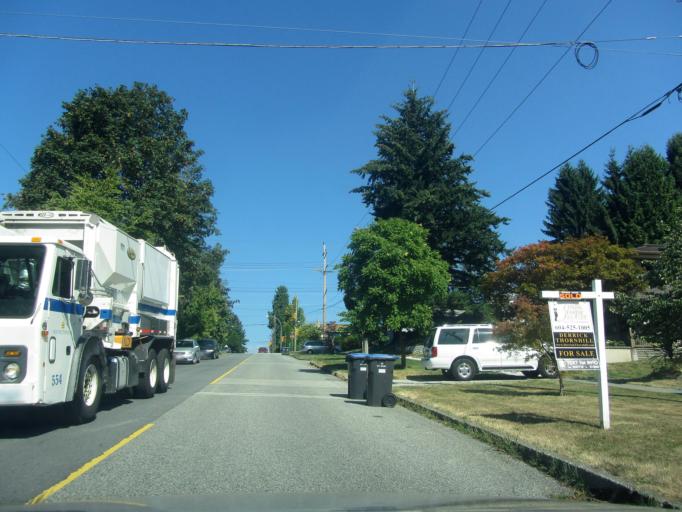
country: CA
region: British Columbia
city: New Westminster
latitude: 49.2216
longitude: -122.9205
